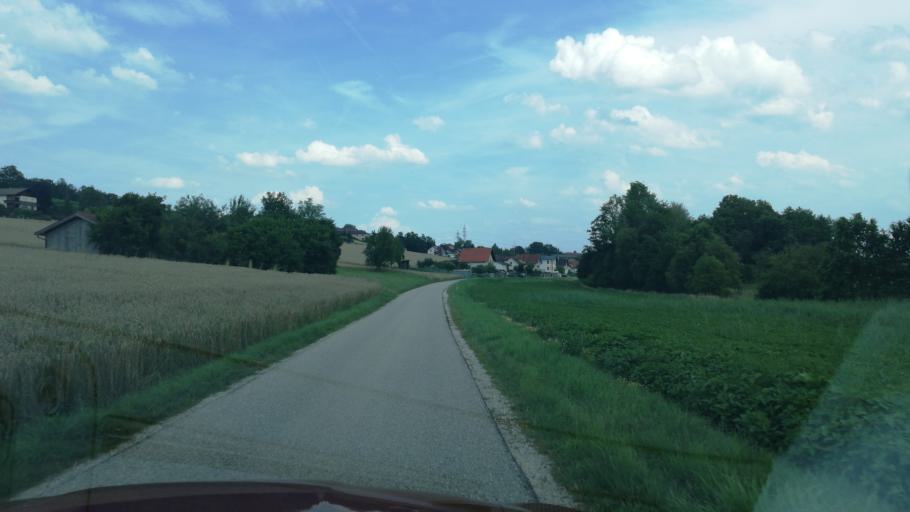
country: AT
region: Upper Austria
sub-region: Wels-Land
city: Lambach
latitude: 48.1038
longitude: 13.8532
